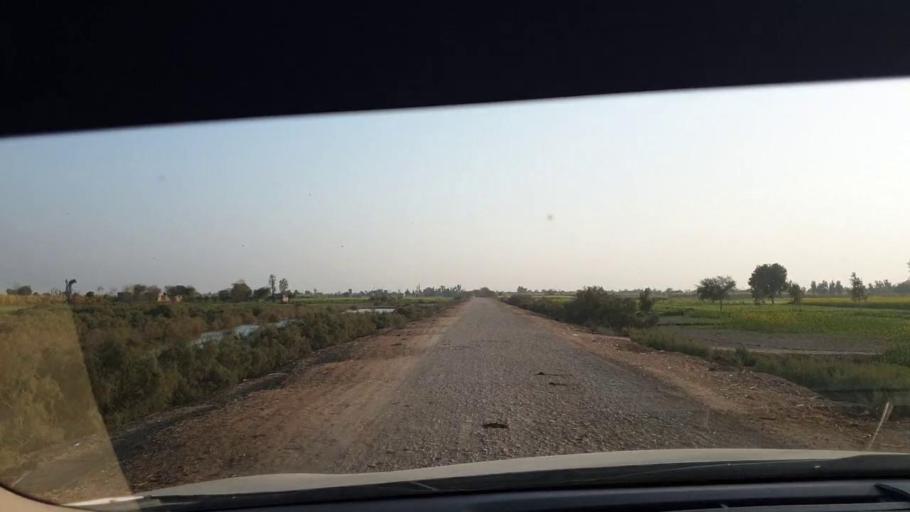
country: PK
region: Sindh
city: Berani
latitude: 25.8461
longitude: 68.8166
